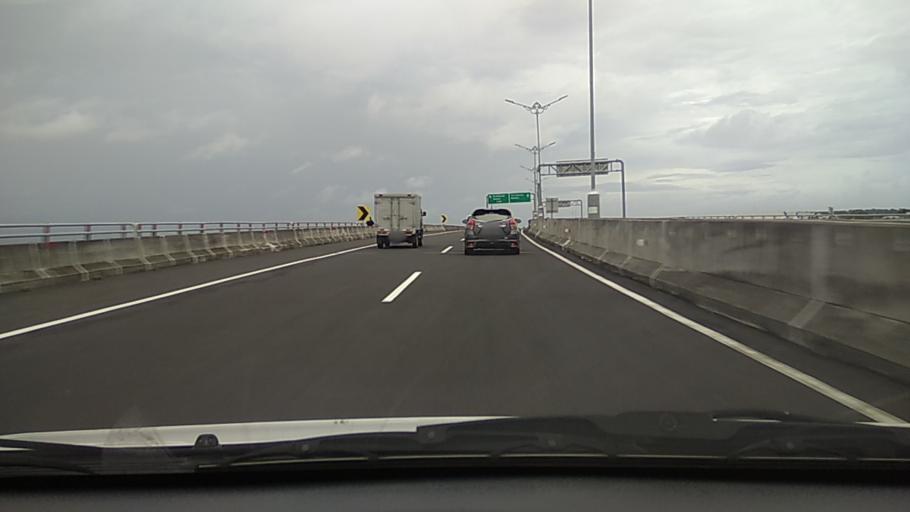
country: ID
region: Bali
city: Jabajero
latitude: -8.7368
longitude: 115.2005
